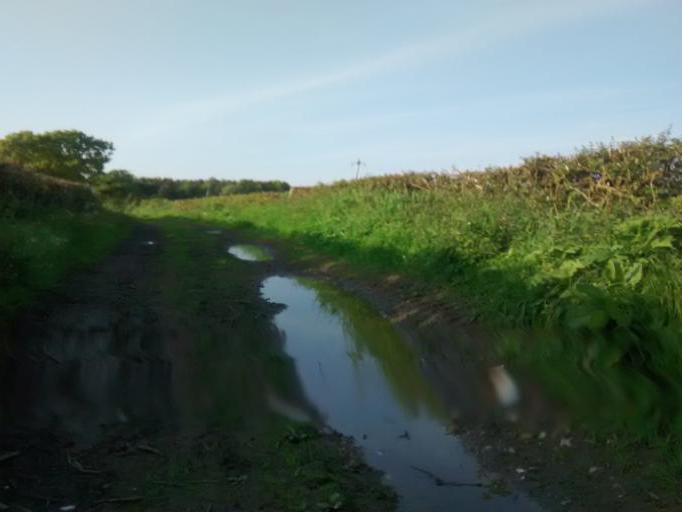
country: GB
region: England
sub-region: County Durham
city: West Cornforth
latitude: 54.7291
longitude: -1.5479
